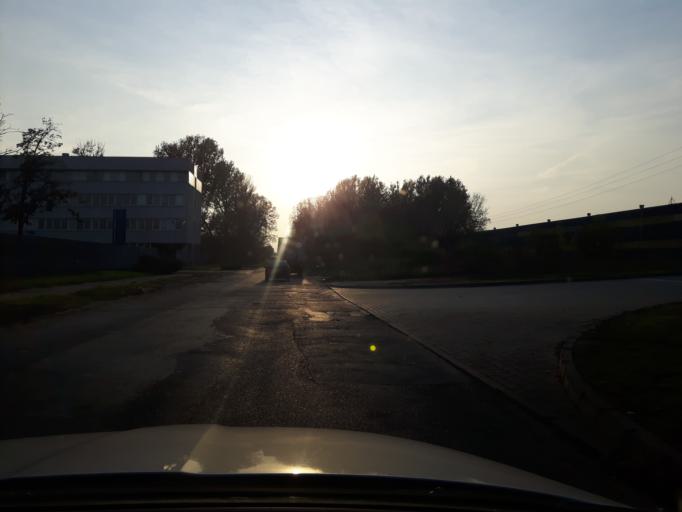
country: PL
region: Masovian Voivodeship
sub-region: Warszawa
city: Praga Poludnie
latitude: 52.2645
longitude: 21.0931
